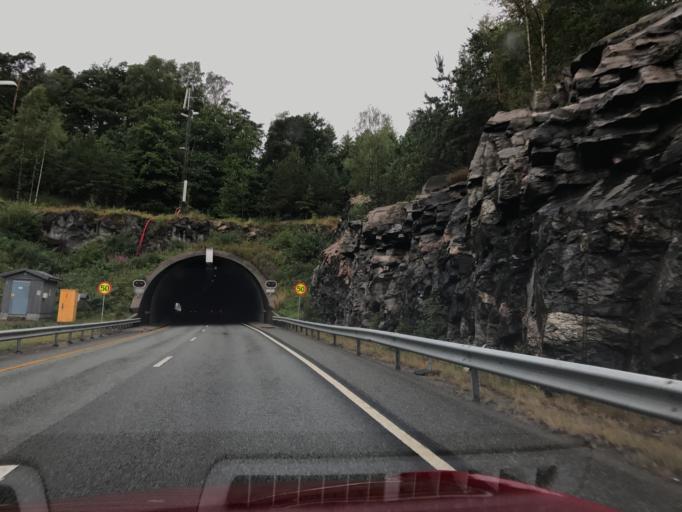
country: NO
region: Vest-Agder
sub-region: Kristiansand
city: Justvik
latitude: 58.1615
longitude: 8.0696
